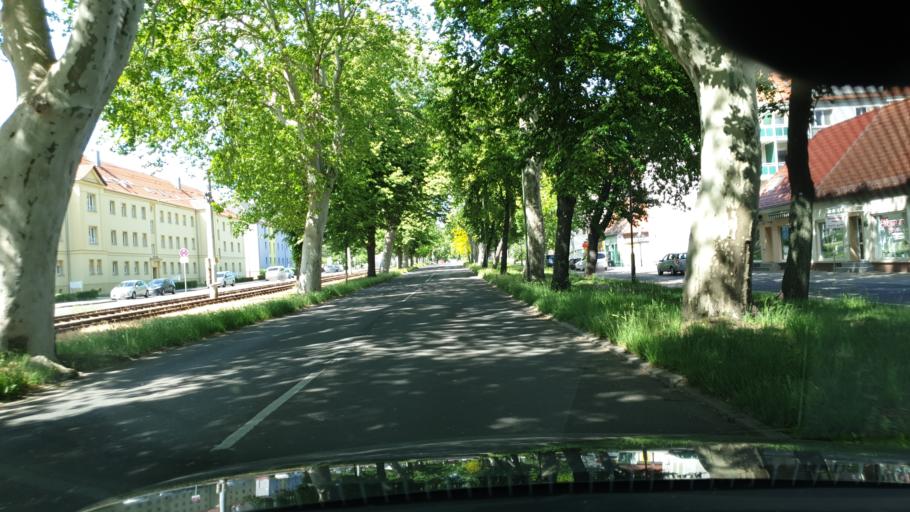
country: DE
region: Saxony-Anhalt
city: Dessau
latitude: 51.8035
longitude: 12.2410
